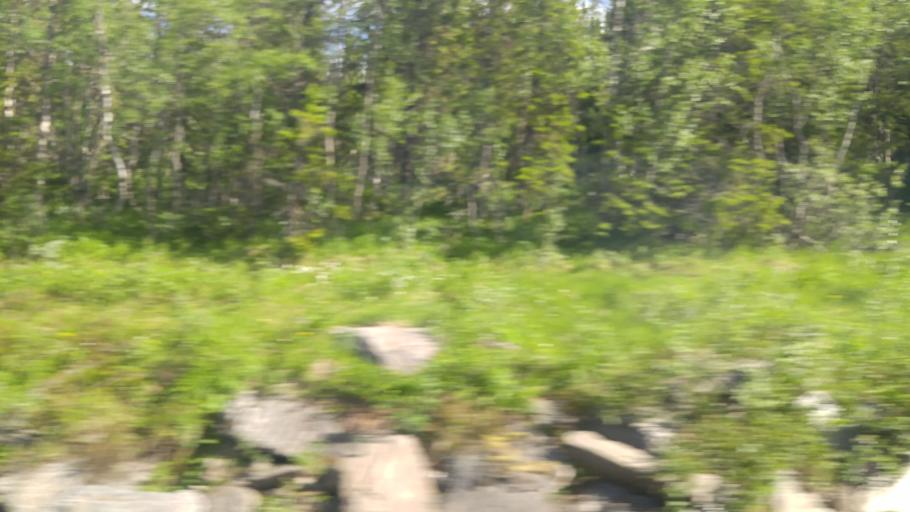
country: NO
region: Nord-Trondelag
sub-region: Meraker
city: Meraker
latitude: 63.2949
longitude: 12.3076
